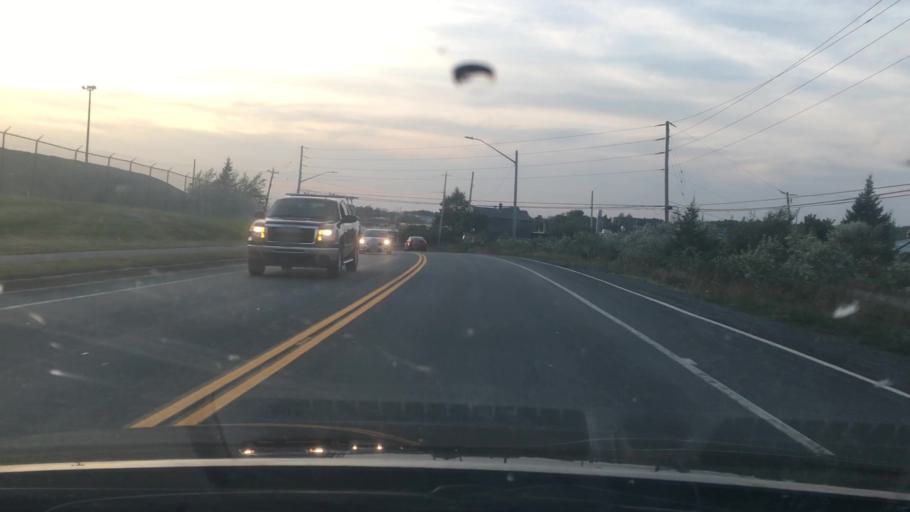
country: CA
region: Nova Scotia
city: Cole Harbour
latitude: 44.6192
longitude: -63.5032
